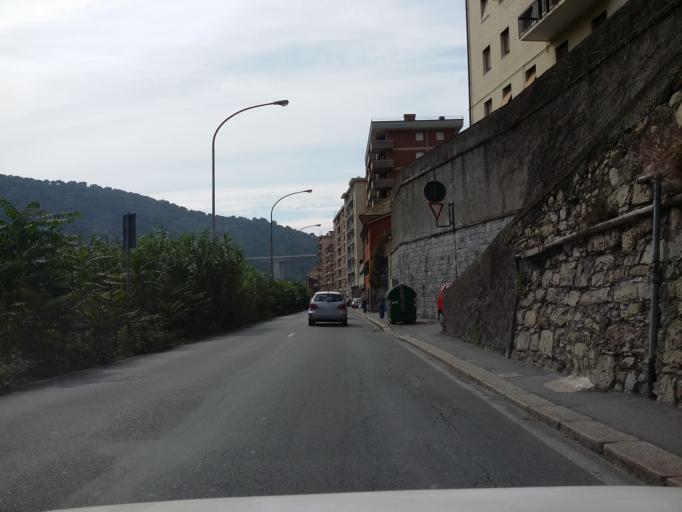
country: IT
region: Liguria
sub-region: Provincia di Genova
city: Piccarello
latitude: 44.4413
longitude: 8.9634
